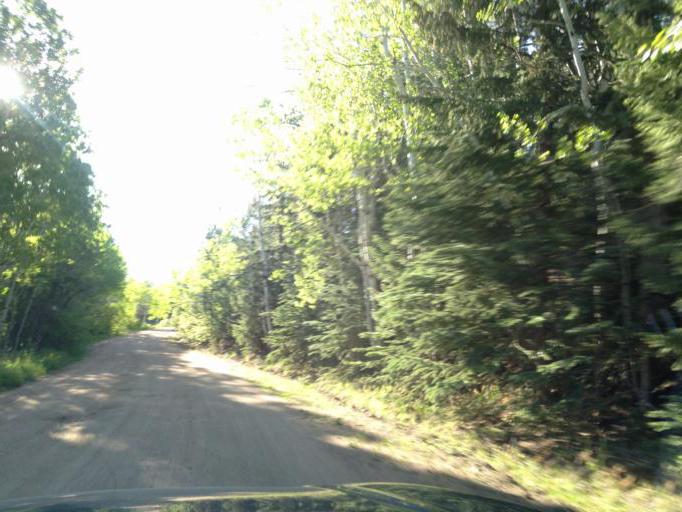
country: US
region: Colorado
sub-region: Jefferson County
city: Evergreen
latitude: 39.4126
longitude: -105.5339
